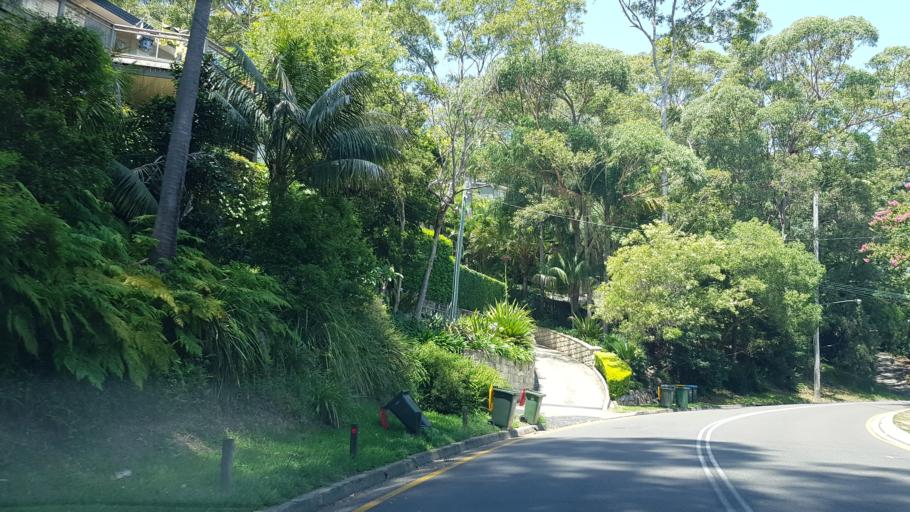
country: AU
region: New South Wales
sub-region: Pittwater
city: Bay View
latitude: -33.6511
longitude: 151.3049
